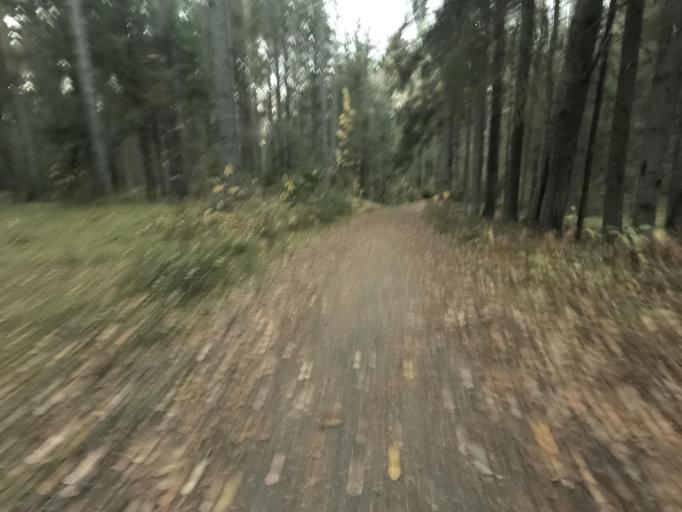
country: RU
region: Leningrad
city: Leninskoye
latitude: 60.1976
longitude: 29.8458
